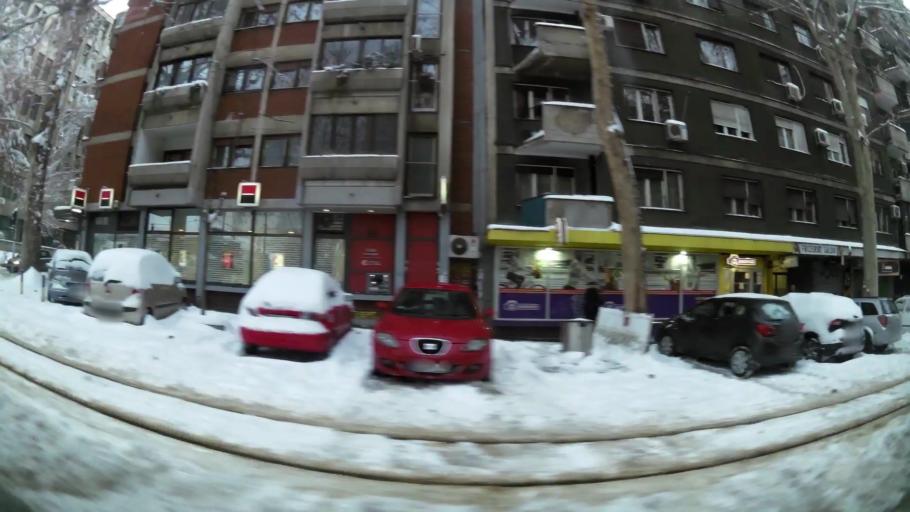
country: RS
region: Central Serbia
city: Belgrade
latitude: 44.8081
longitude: 20.4764
